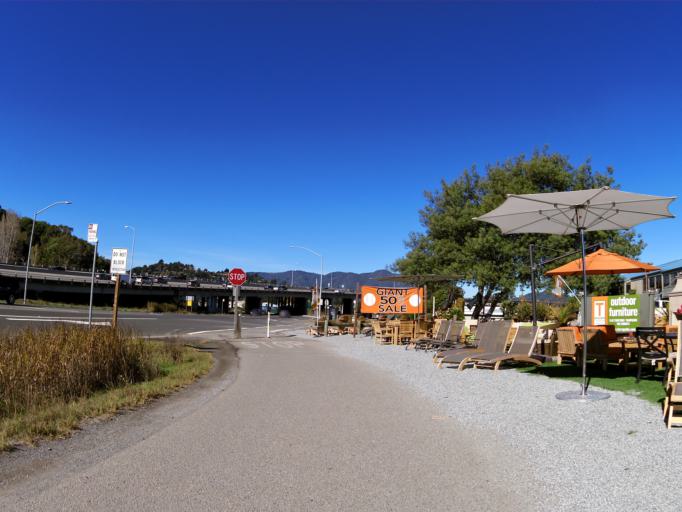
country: US
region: California
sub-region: Marin County
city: Marin City
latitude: 37.8793
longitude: -122.5145
